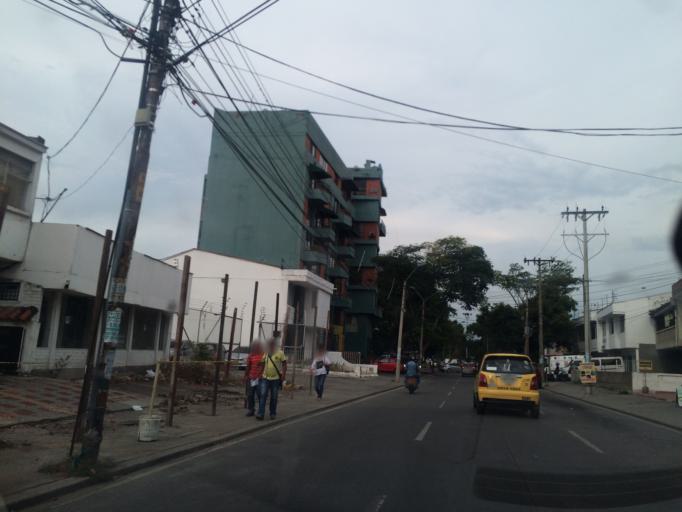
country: CO
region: Valle del Cauca
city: Cali
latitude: 3.4649
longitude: -76.5259
